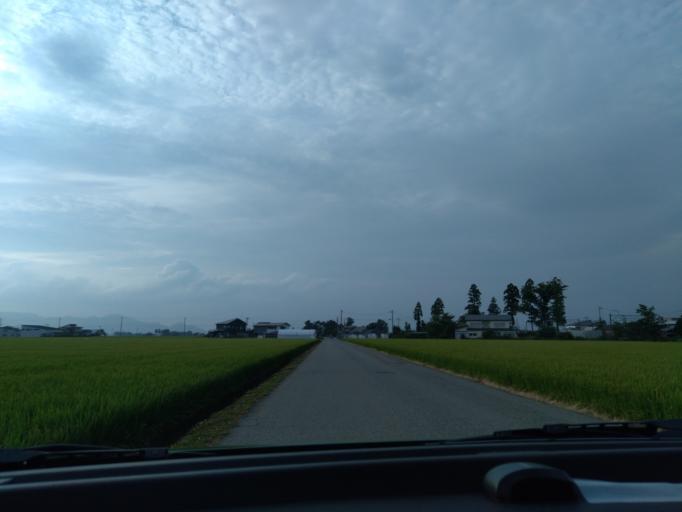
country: JP
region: Akita
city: Omagari
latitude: 39.4059
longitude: 140.5143
